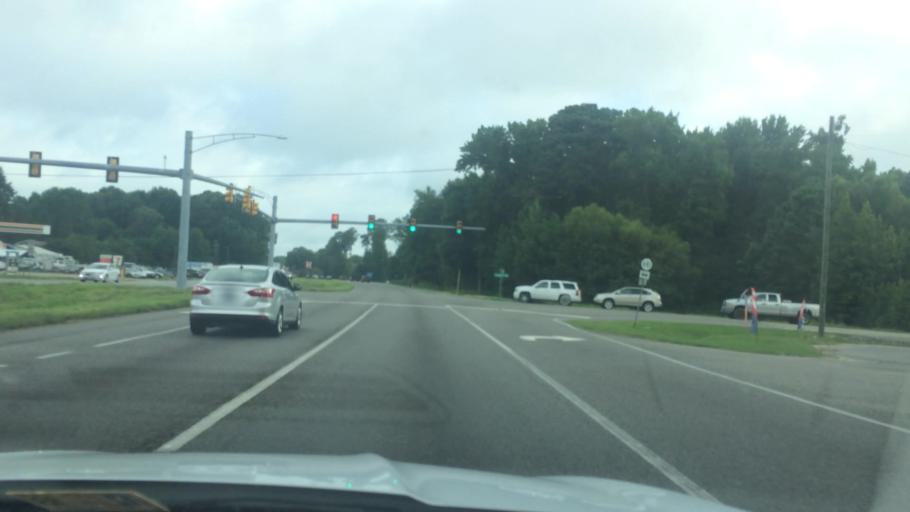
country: US
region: Virginia
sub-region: Gloucester County
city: Gloucester Point
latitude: 37.2682
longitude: -76.4944
